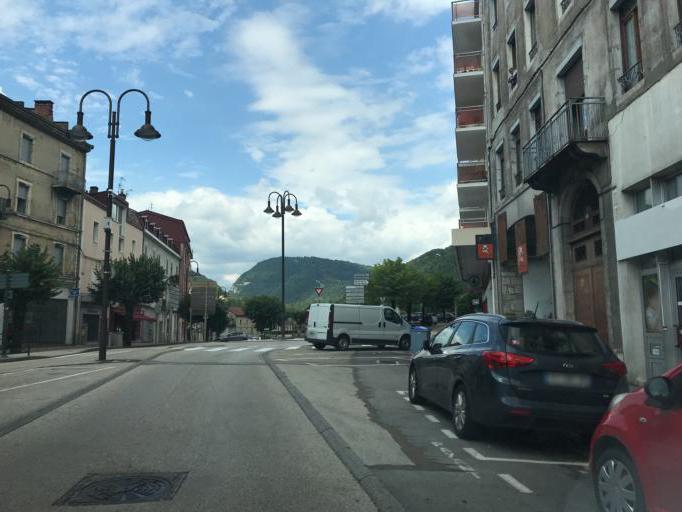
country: FR
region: Franche-Comte
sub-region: Departement du Jura
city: Saint-Claude
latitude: 46.3922
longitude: 5.8642
